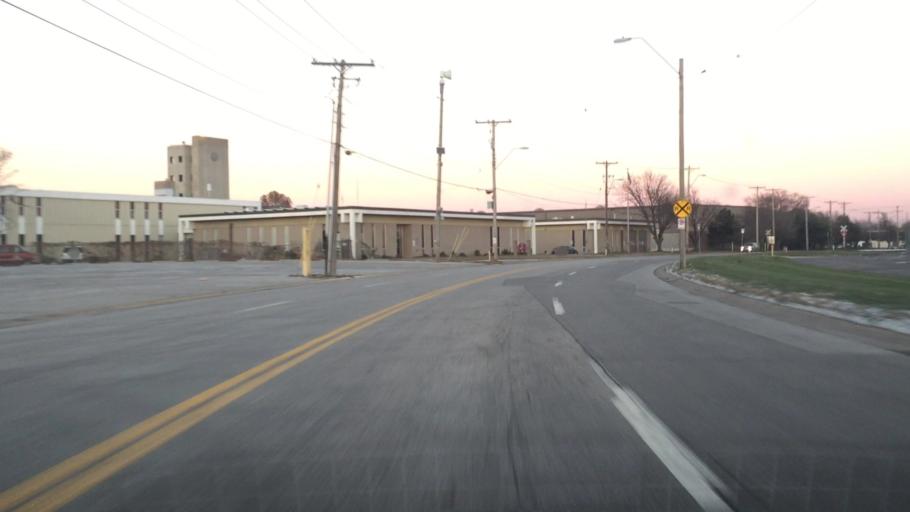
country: US
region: Missouri
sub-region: Clay County
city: North Kansas City
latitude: 39.1394
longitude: -94.5214
